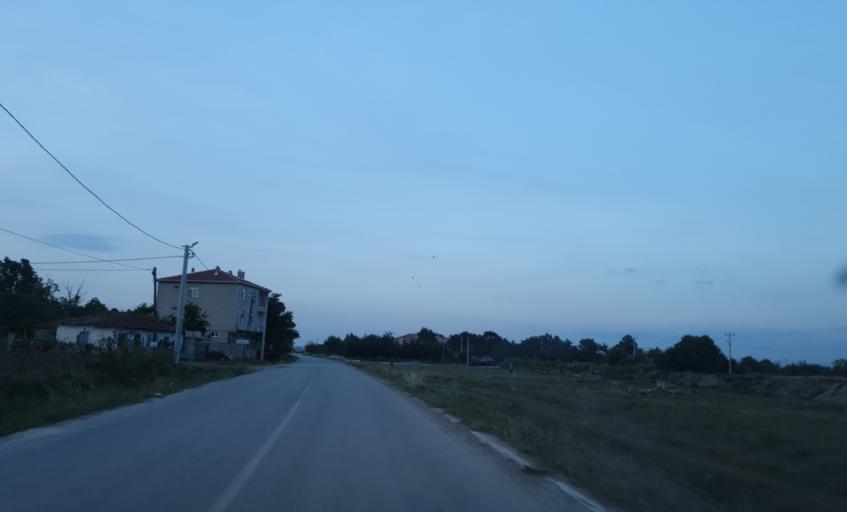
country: TR
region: Tekirdag
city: Beyazkoy
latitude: 41.4360
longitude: 27.6960
